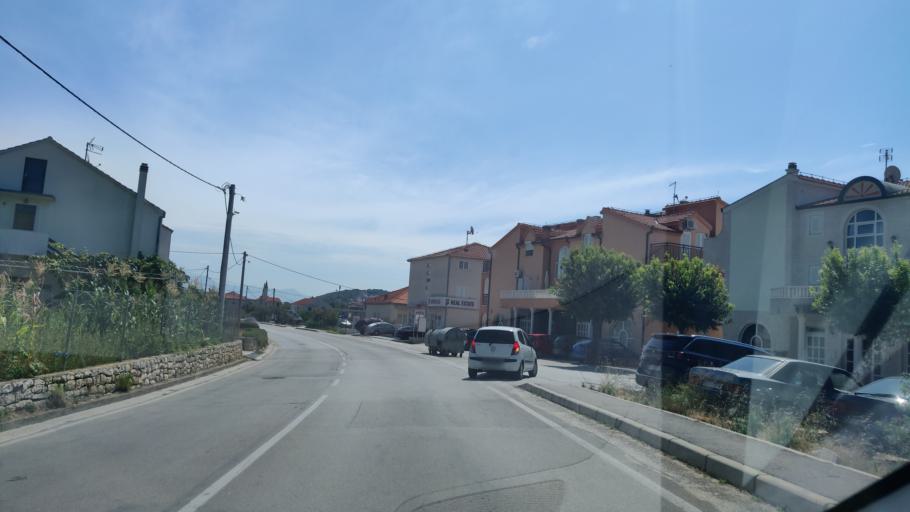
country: HR
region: Splitsko-Dalmatinska
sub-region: Grad Trogir
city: Trogir
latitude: 43.5175
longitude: 16.2384
